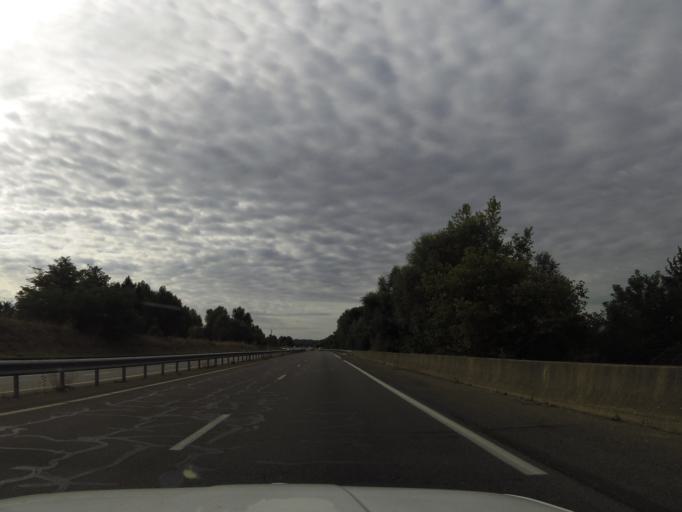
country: FR
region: Languedoc-Roussillon
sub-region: Departement du Gard
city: Saint-Hilaire-de-Brethmas
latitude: 44.0892
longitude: 4.1070
